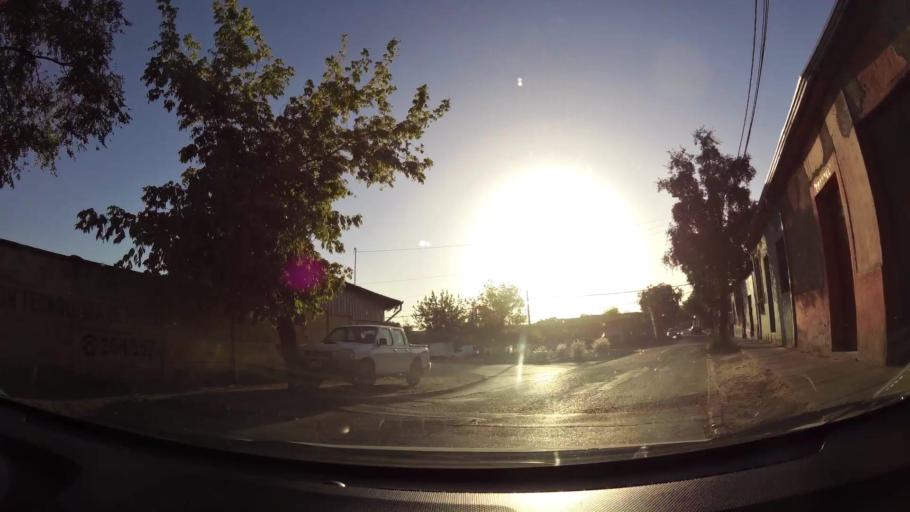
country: CL
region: Maule
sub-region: Provincia de Talca
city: Talca
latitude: -35.4387
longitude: -71.6459
